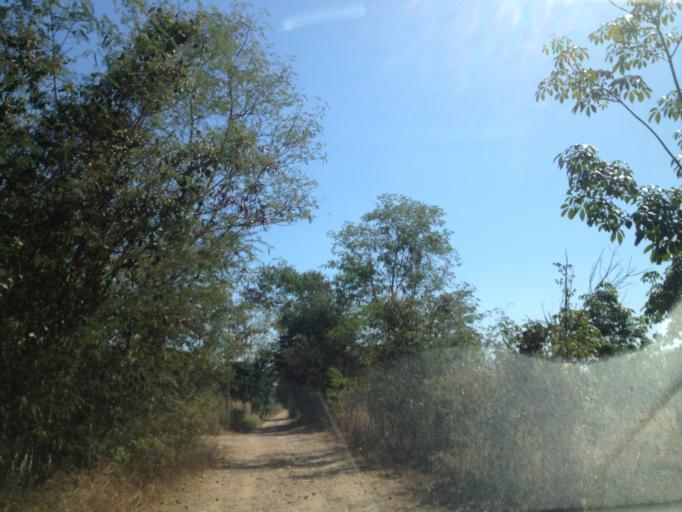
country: TH
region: Chiang Mai
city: San Pa Tong
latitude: 18.6733
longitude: 98.8679
